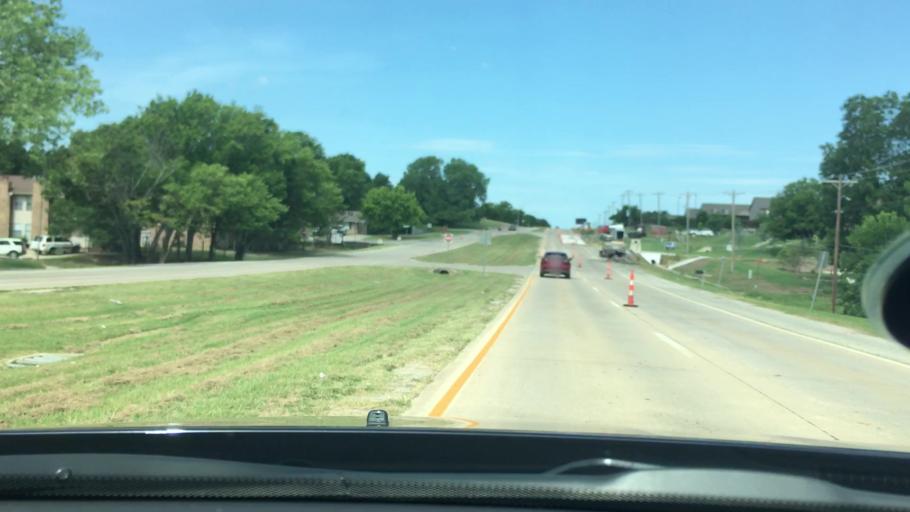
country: US
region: Oklahoma
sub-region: Pontotoc County
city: Ada
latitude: 34.7816
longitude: -96.6405
